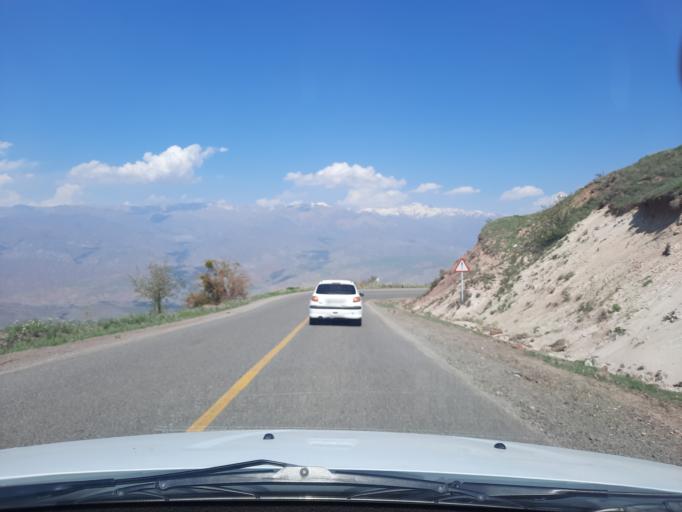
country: IR
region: Qazvin
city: Qazvin
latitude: 36.4136
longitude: 50.2389
